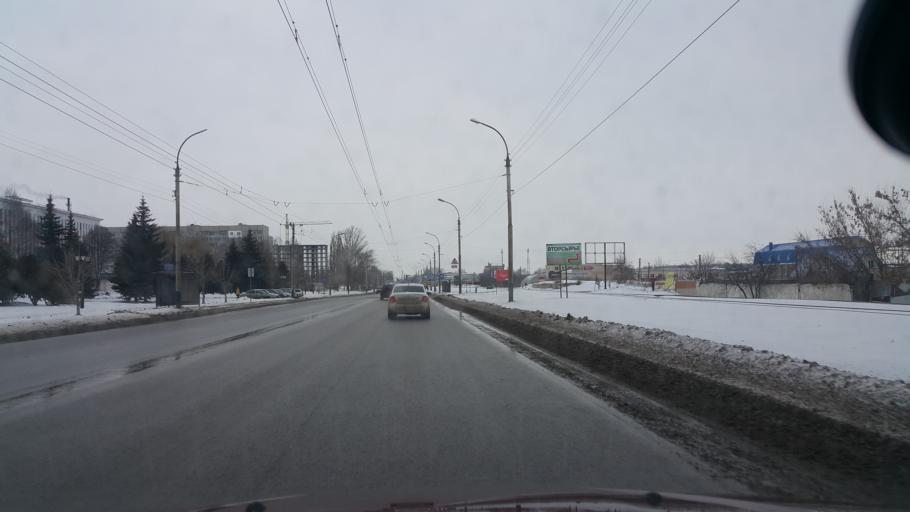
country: RU
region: Tambov
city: Tambov
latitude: 52.7369
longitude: 41.3845
